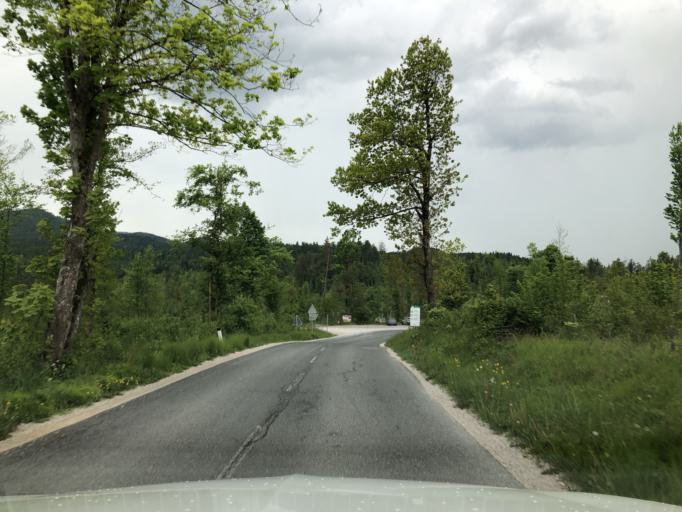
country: SI
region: Cerknica
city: Rakek
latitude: 45.8057
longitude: 14.2809
